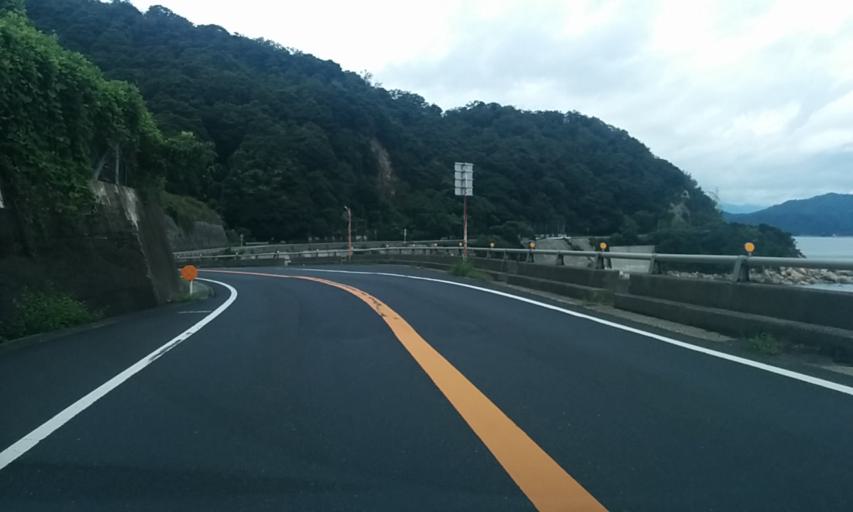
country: JP
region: Kyoto
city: Miyazu
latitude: 35.5293
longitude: 135.2708
